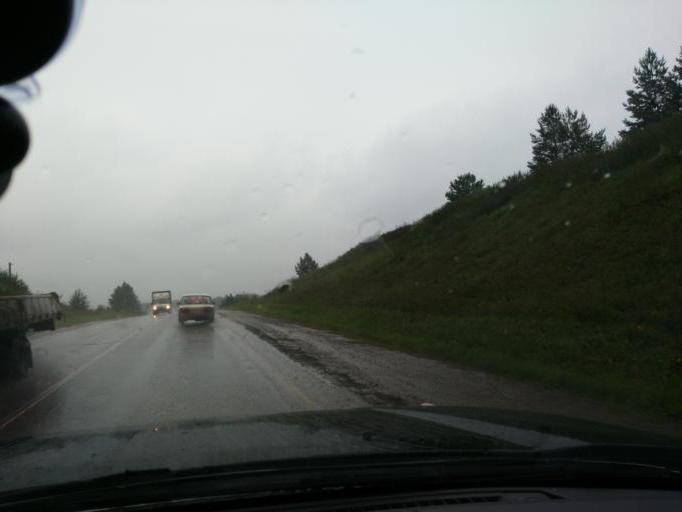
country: RU
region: Perm
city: Osa
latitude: 57.1927
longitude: 55.5914
